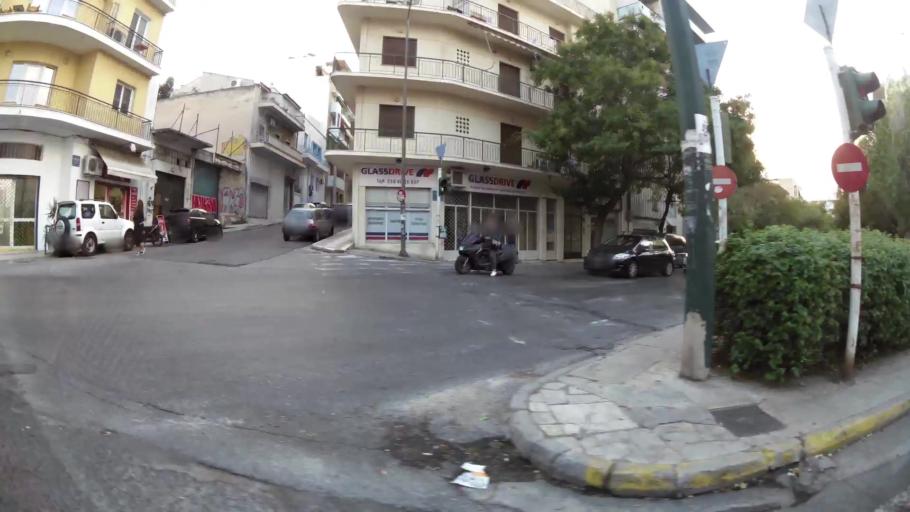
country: GR
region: Attica
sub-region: Nomarchia Athinas
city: Dhafni
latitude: 37.9573
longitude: 23.7316
